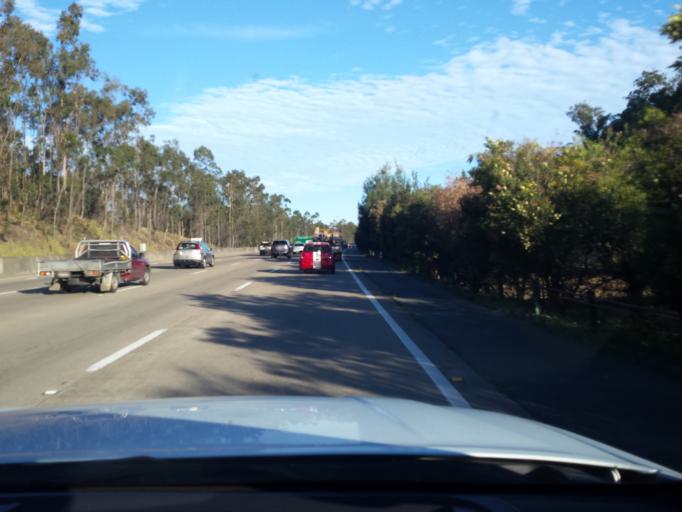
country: AU
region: Queensland
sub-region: Gold Coast
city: Ormeau Hills
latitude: -27.8244
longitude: 153.2959
